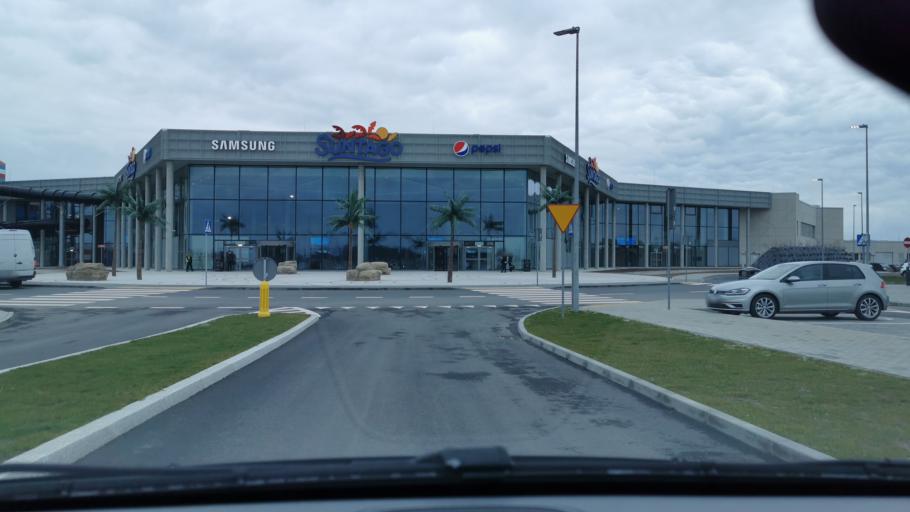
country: PL
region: Masovian Voivodeship
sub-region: Powiat zyrardowski
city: Mszczonow
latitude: 51.9876
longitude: 20.4613
